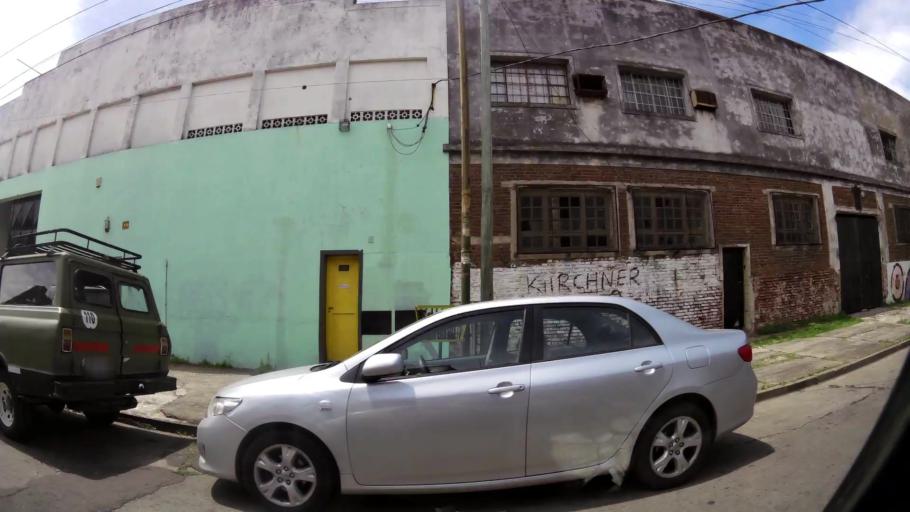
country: AR
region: Buenos Aires
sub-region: Partido de Lanus
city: Lanus
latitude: -34.6704
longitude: -58.4012
